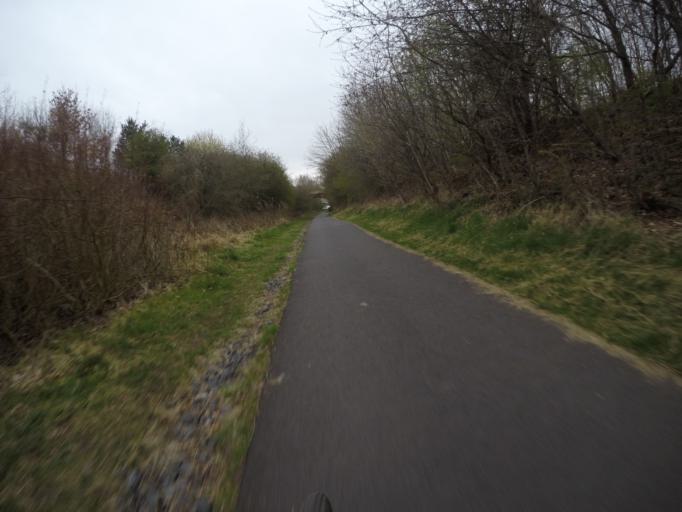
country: GB
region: Scotland
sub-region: North Ayrshire
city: Dreghorn
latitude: 55.6092
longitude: -4.6333
